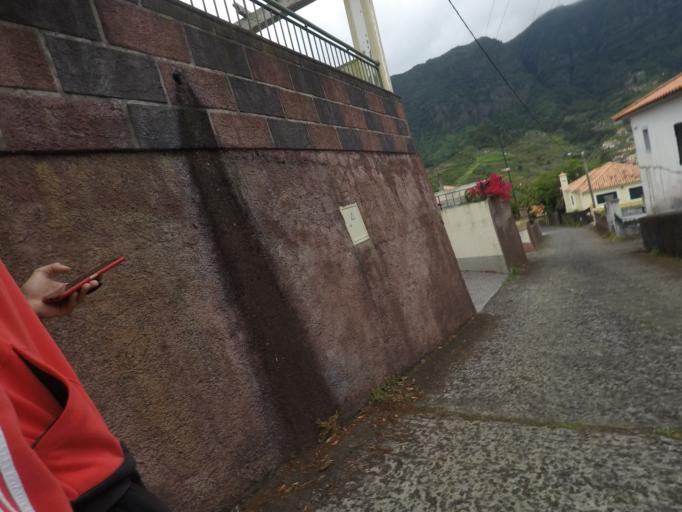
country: PT
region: Madeira
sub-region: Sao Vicente
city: Sao Vicente
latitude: 32.7887
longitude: -17.0377
